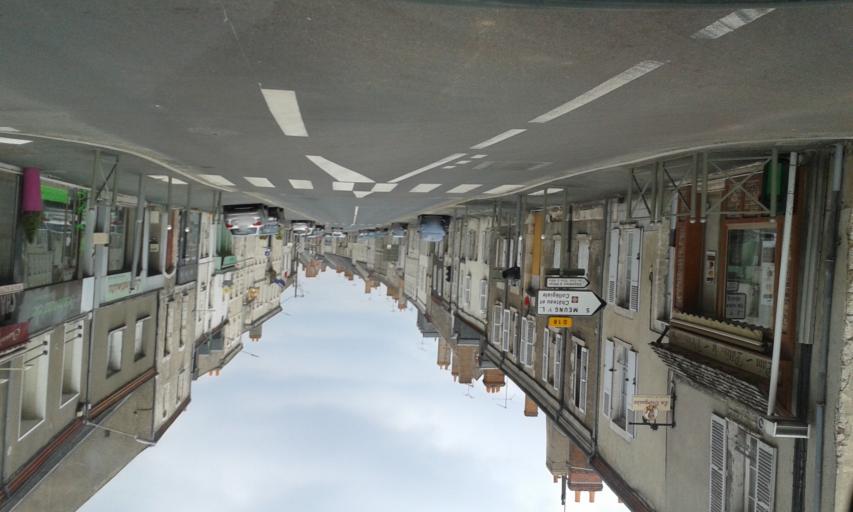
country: FR
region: Centre
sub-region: Departement du Loiret
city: Clery-Saint-Andre
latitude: 47.8207
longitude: 1.7552
